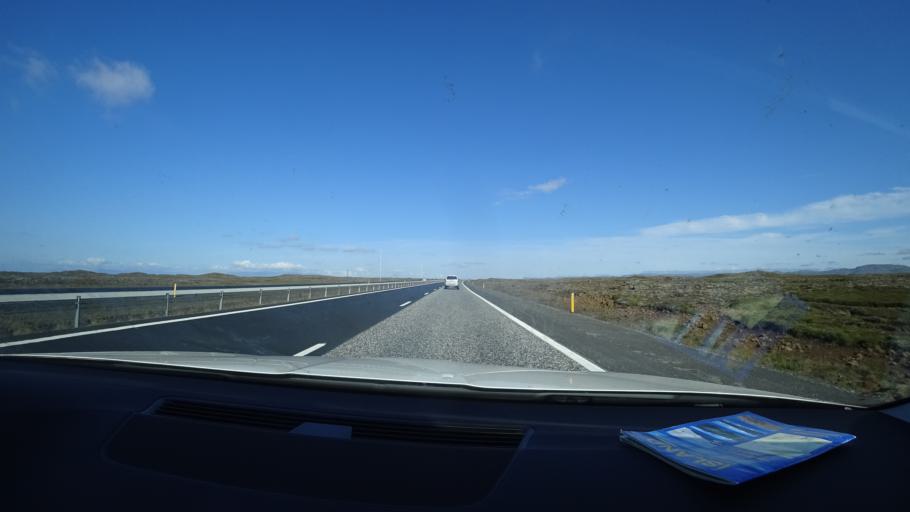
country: IS
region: Southern Peninsula
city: Vogar
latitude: 63.9972
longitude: -22.2617
